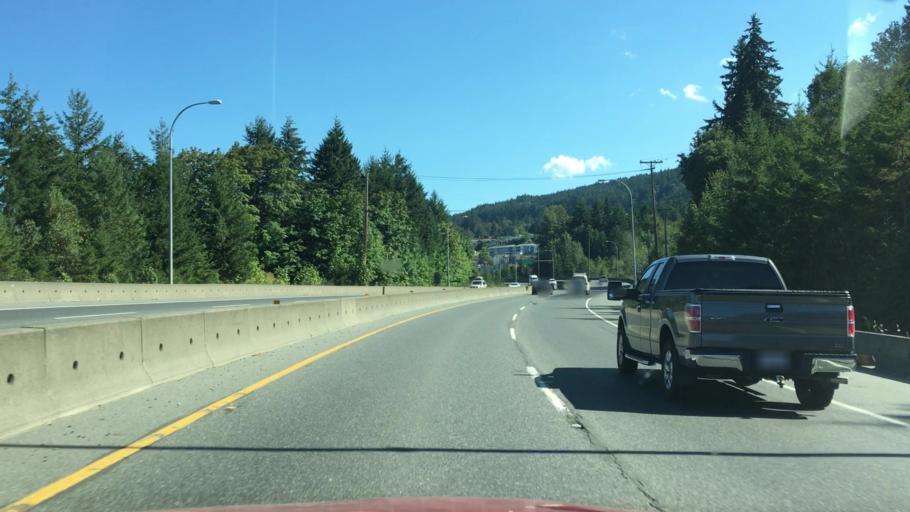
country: CA
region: British Columbia
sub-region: Cowichan Valley Regional District
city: Ladysmith
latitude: 48.9834
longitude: -123.8056
